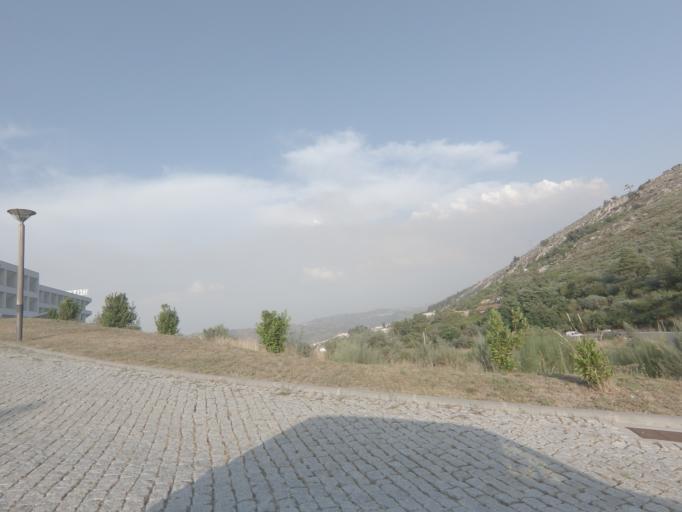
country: PT
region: Viseu
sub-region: Tabuaco
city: Tabuaco
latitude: 41.1190
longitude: -7.5840
